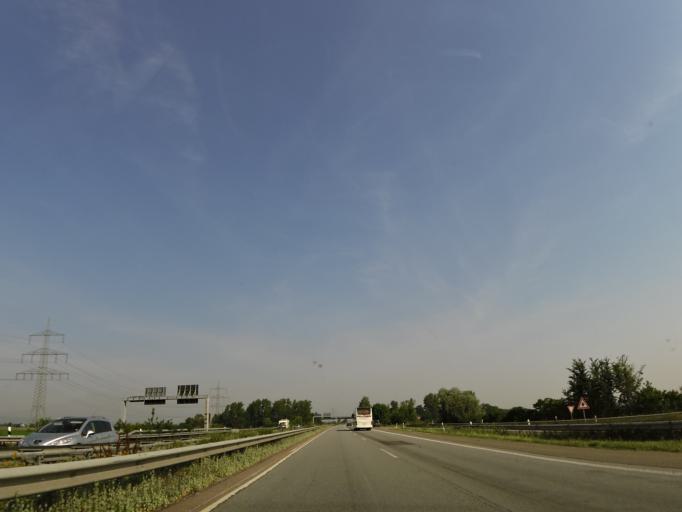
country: DE
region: Rheinland-Pfalz
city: Dannstadt-Schauernheim
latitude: 49.4442
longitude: 8.3230
